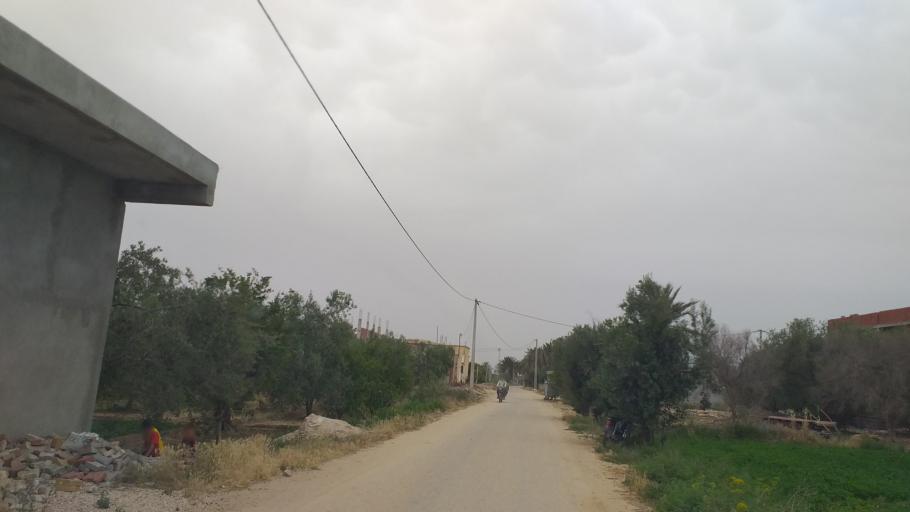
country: TN
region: Qabis
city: Gabes
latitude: 33.9543
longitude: 10.0597
